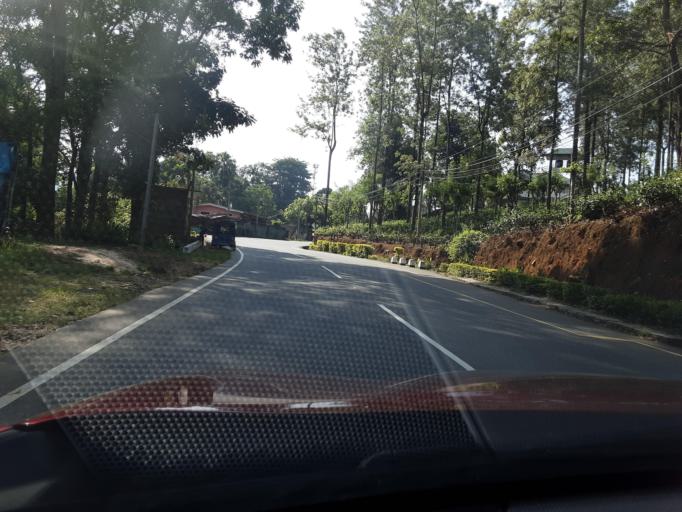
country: LK
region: Uva
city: Badulla
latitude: 6.9800
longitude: 81.0806
